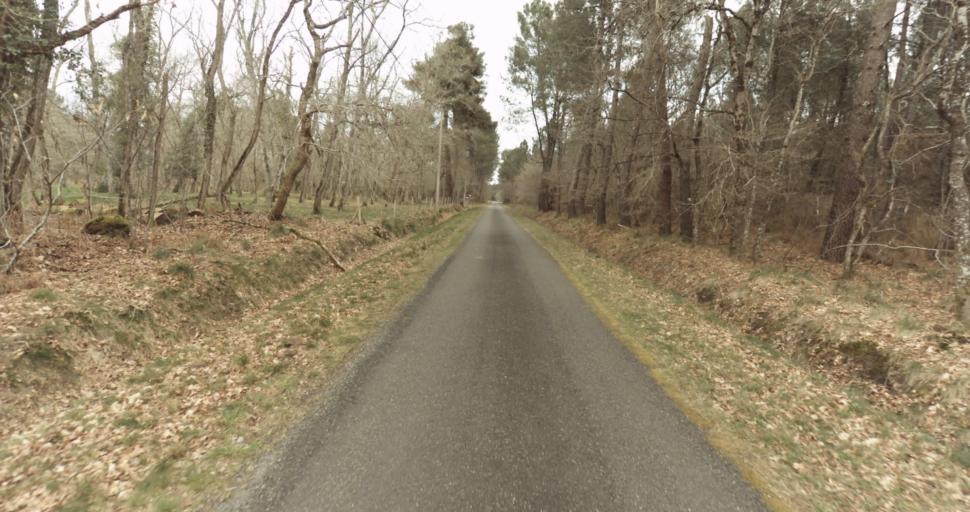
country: FR
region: Aquitaine
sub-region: Departement des Landes
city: Roquefort
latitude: 44.0762
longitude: -0.3801
